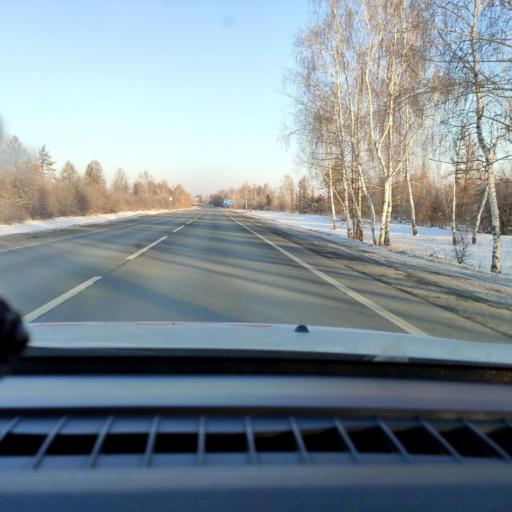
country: RU
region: Samara
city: Bereza
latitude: 53.4789
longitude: 50.1167
